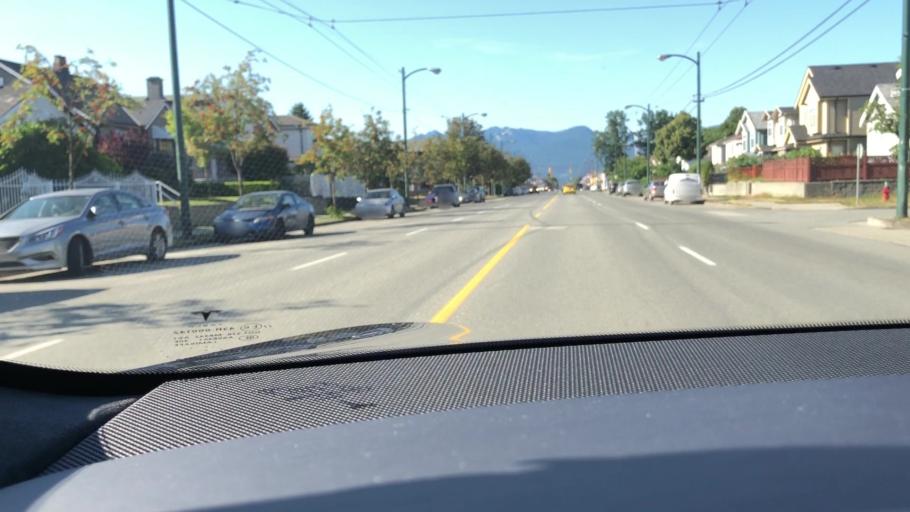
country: CA
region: British Columbia
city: Vancouver
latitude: 49.2282
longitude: -123.0657
